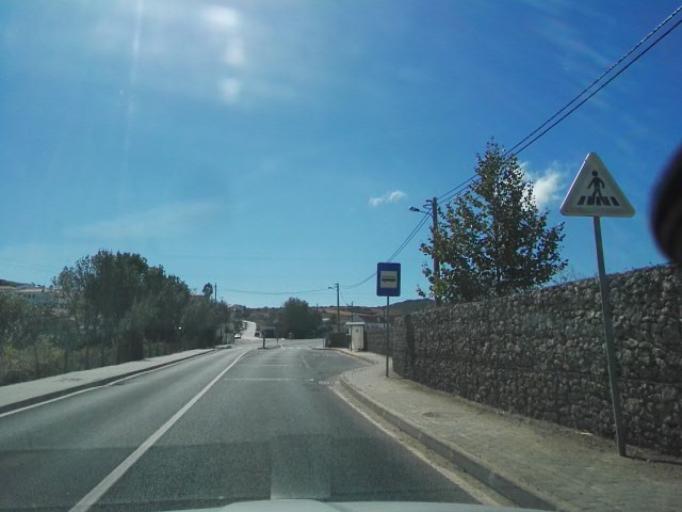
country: PT
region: Lisbon
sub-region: Arruda Dos Vinhos
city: Arruda dos Vinhos
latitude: 38.9600
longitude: -9.0597
